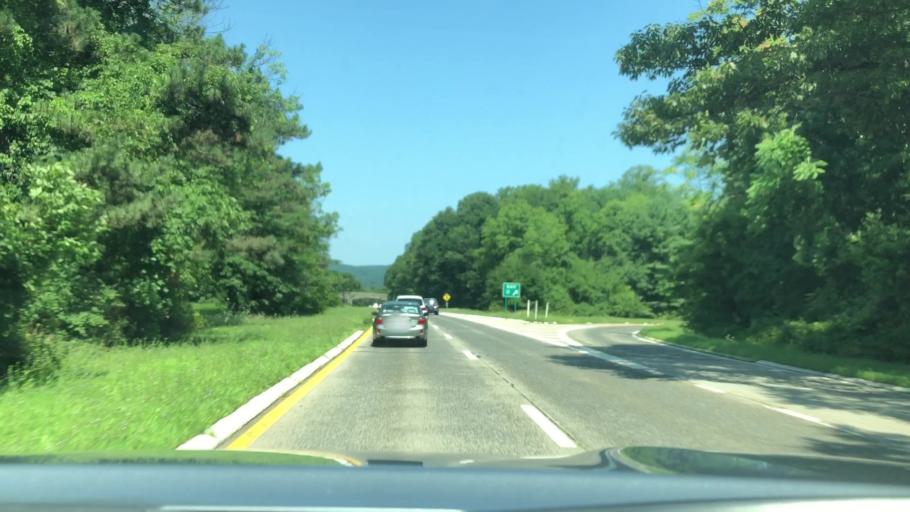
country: US
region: New York
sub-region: Rockland County
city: Pomona
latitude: 41.1693
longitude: -74.0305
